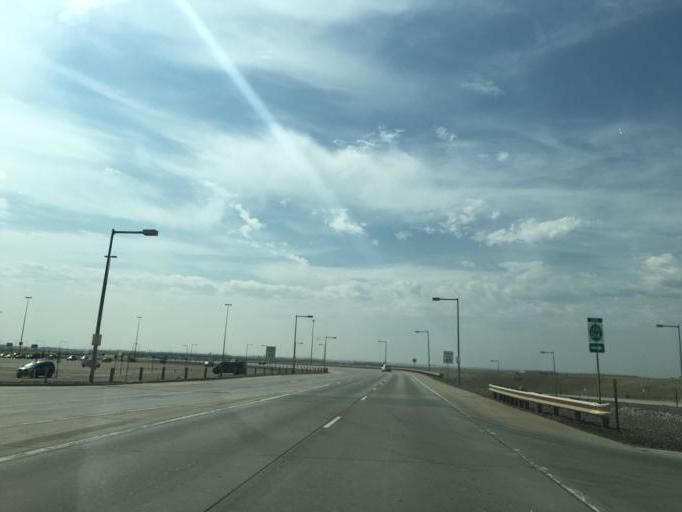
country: US
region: Colorado
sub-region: Weld County
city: Lochbuie
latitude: 39.8486
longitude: -104.6821
